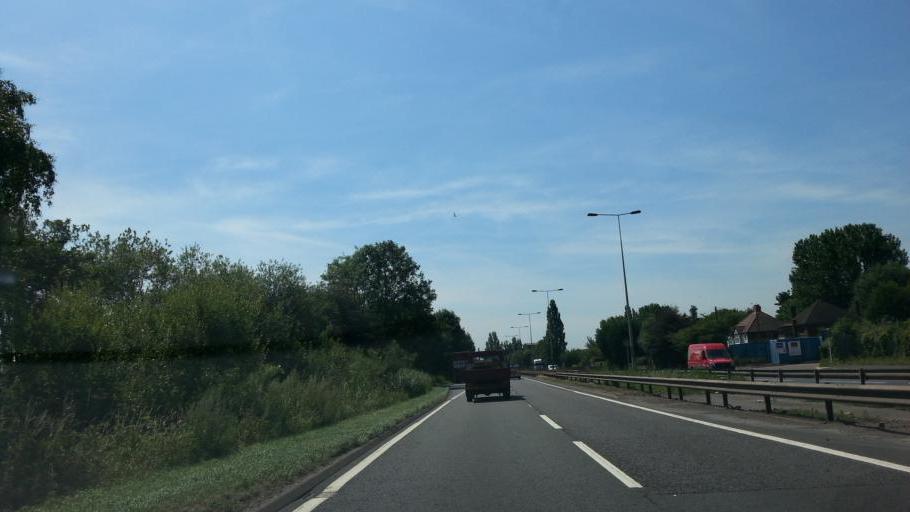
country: GB
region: England
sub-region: Staffordshire
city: Burton upon Trent
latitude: 52.7839
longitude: -1.6780
